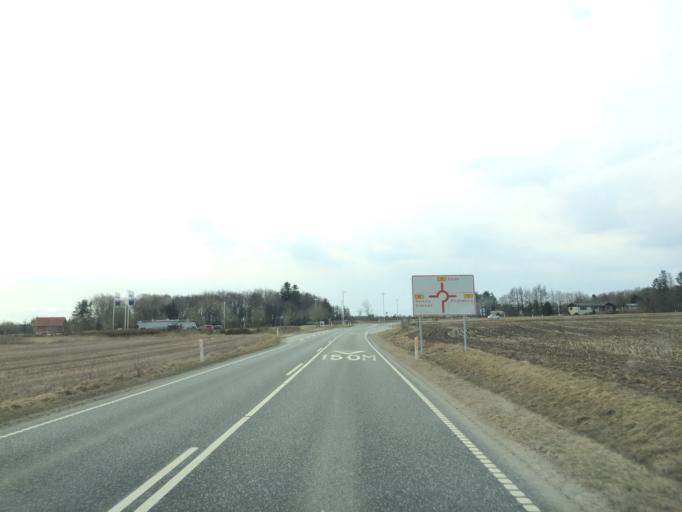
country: DK
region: Central Jutland
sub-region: Ringkobing-Skjern Kommune
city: Videbaek
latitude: 56.0879
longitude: 8.5073
